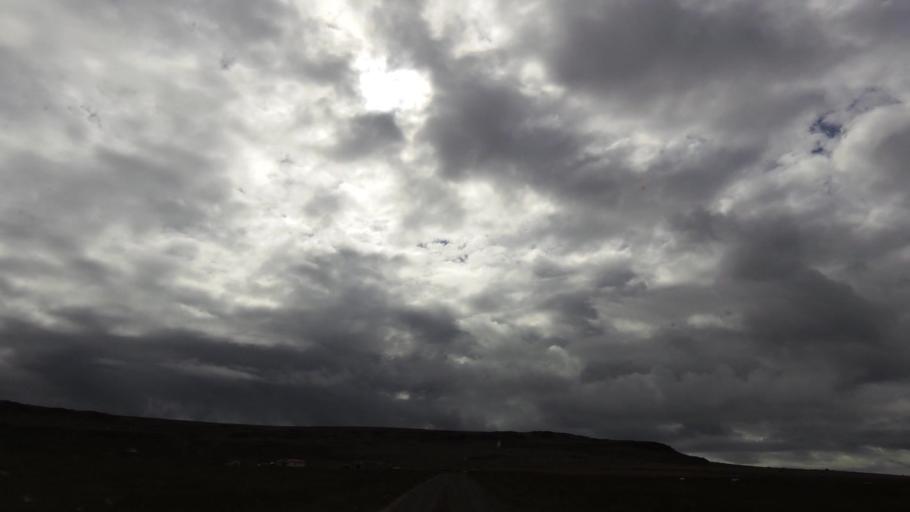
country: IS
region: West
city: Olafsvik
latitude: 65.6061
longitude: -24.3431
